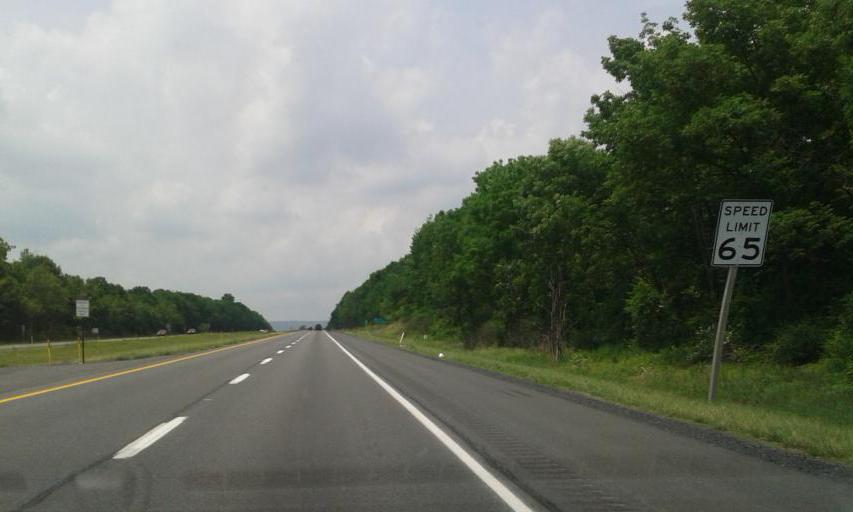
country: US
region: Pennsylvania
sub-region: Northampton County
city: Belfast
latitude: 40.7840
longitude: -75.2856
